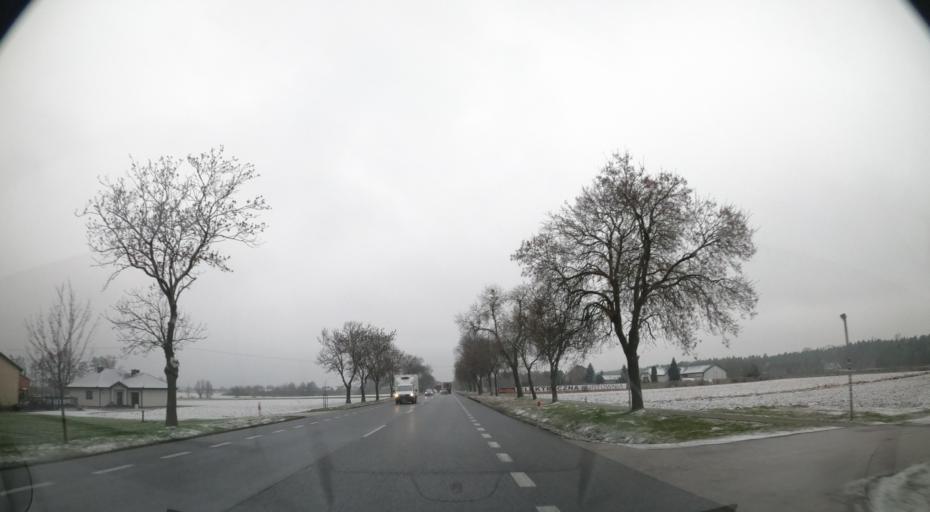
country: PL
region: Masovian Voivodeship
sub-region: Powiat sochaczewski
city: Sochaczew
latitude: 52.2239
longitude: 20.2990
